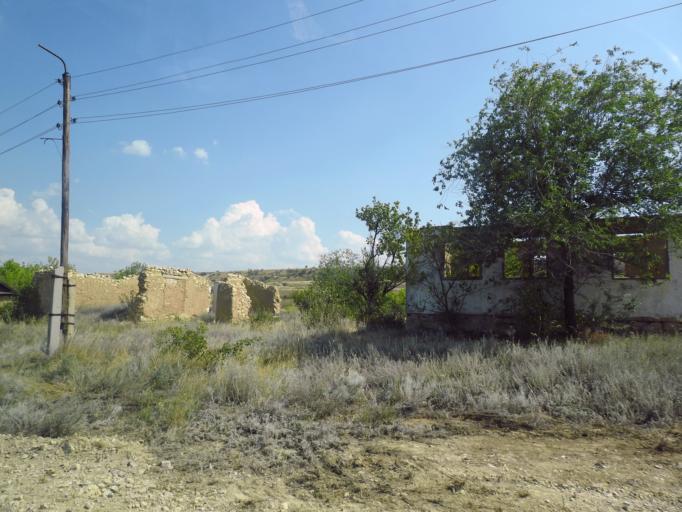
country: RU
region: Saratov
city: Rovnoye
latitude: 50.5097
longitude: 45.7595
